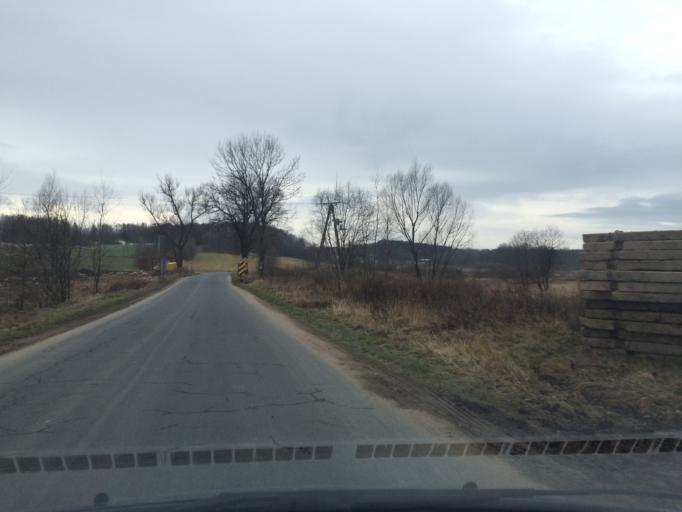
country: PL
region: Lower Silesian Voivodeship
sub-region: Powiat lwowecki
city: Lwowek Slaski
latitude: 51.1207
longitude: 15.5344
